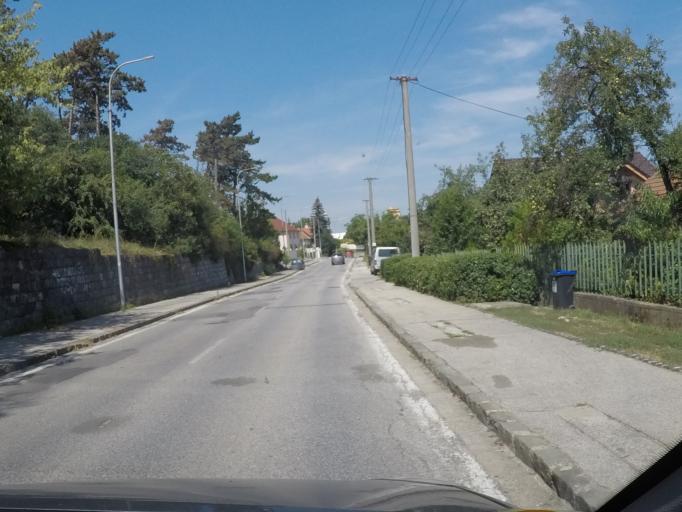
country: SK
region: Nitriansky
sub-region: Okres Nitra
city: Nitra
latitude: 48.3031
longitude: 18.0762
